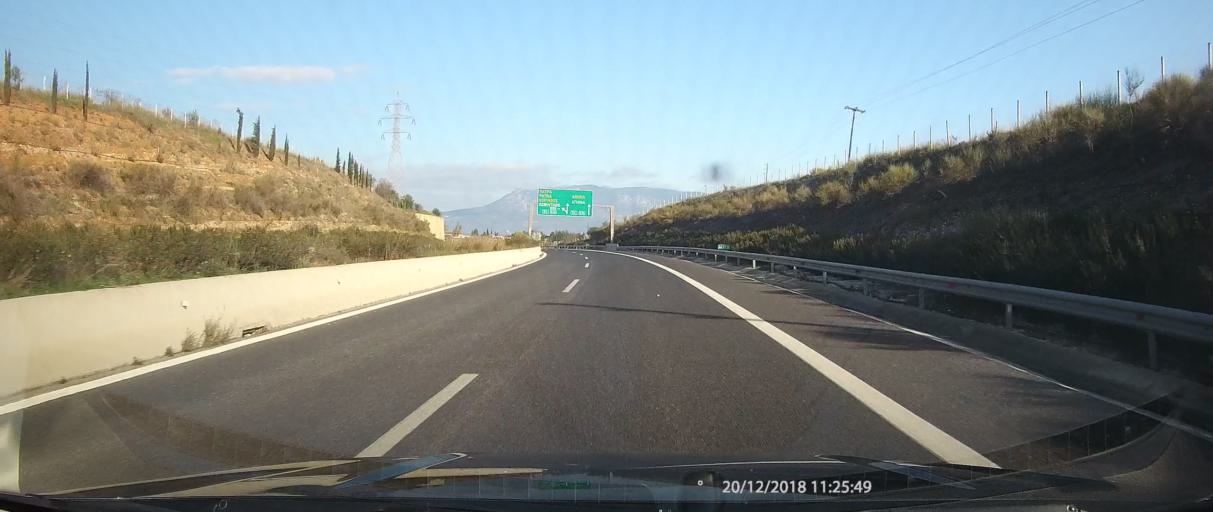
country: GR
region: Peloponnese
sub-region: Nomos Korinthias
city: Arkhaia Korinthos
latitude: 37.9050
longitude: 22.9050
